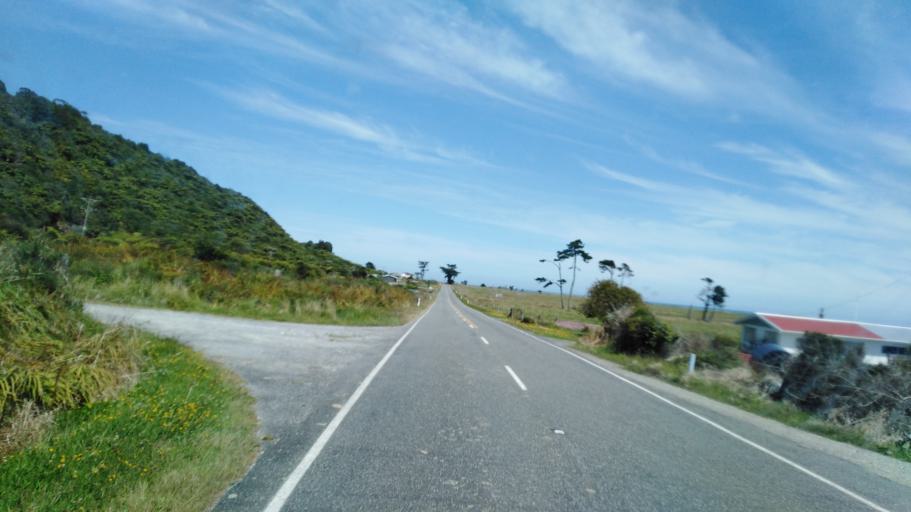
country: NZ
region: West Coast
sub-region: Buller District
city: Westport
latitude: -41.5338
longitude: 171.9362
